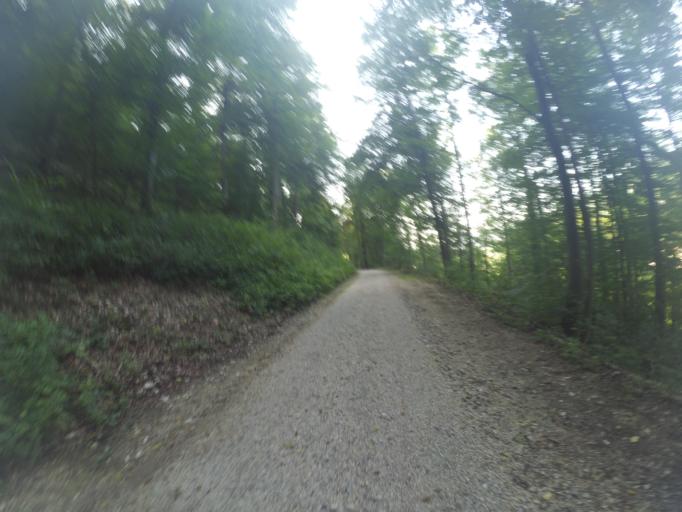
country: DE
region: Baden-Wuerttemberg
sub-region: Tuebingen Region
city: Bad Urach
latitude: 48.4965
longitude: 9.3798
